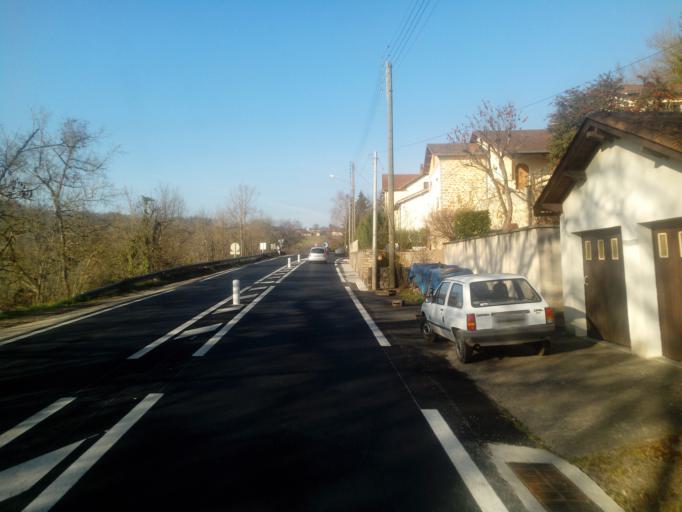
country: FR
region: Midi-Pyrenees
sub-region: Departement de l'Aveyron
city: Capdenac-Gare
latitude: 44.5811
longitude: 2.0665
